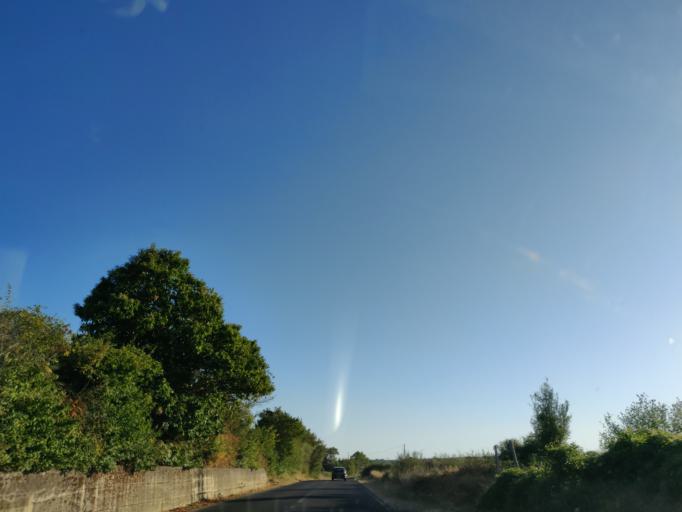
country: IT
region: Latium
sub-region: Provincia di Viterbo
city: Grotte di Castro
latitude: 42.6669
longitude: 11.8565
